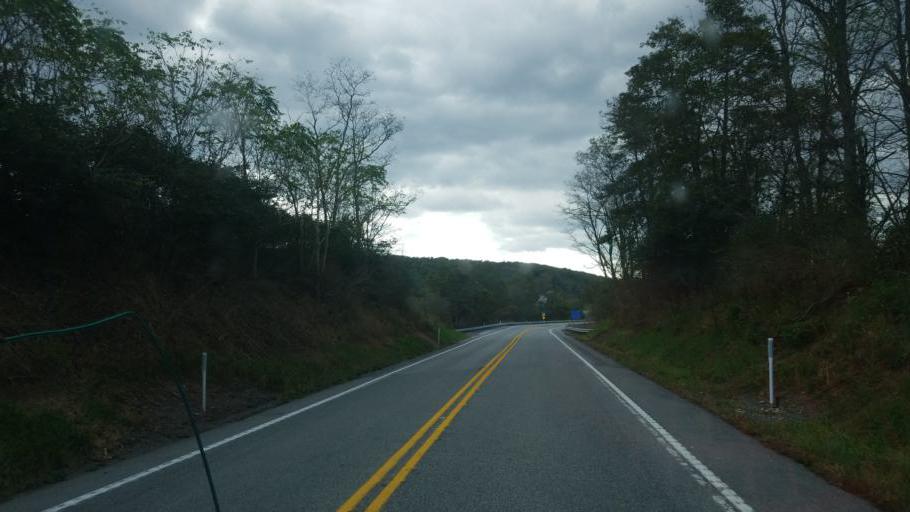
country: US
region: Pennsylvania
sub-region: Fulton County
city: McConnellsburg
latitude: 39.9491
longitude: -78.0220
